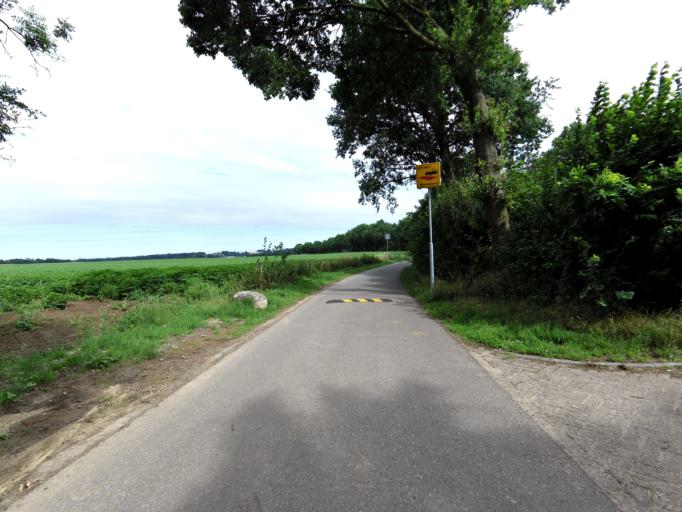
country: NL
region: Limburg
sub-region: Gemeente Schinnen
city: Amstenrade
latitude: 50.9371
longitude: 5.9169
